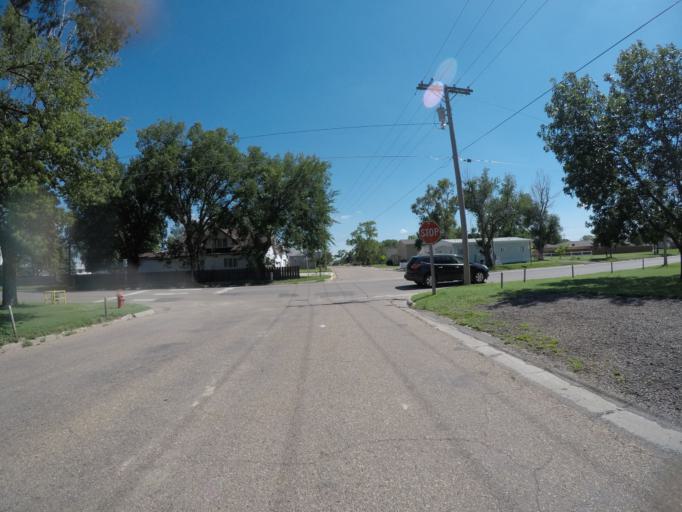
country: US
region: Kansas
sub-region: Sheridan County
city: Hoxie
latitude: 39.3579
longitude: -100.4347
